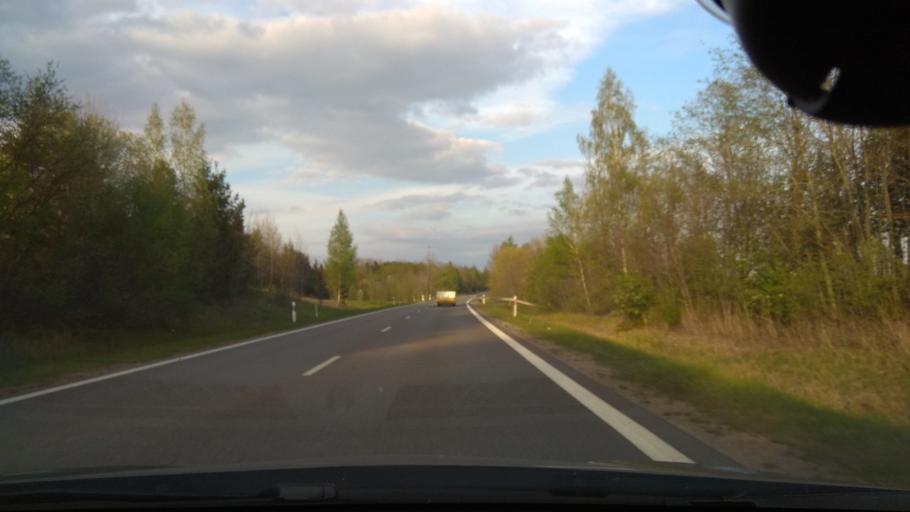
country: LT
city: Jieznas
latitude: 54.5806
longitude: 24.1526
